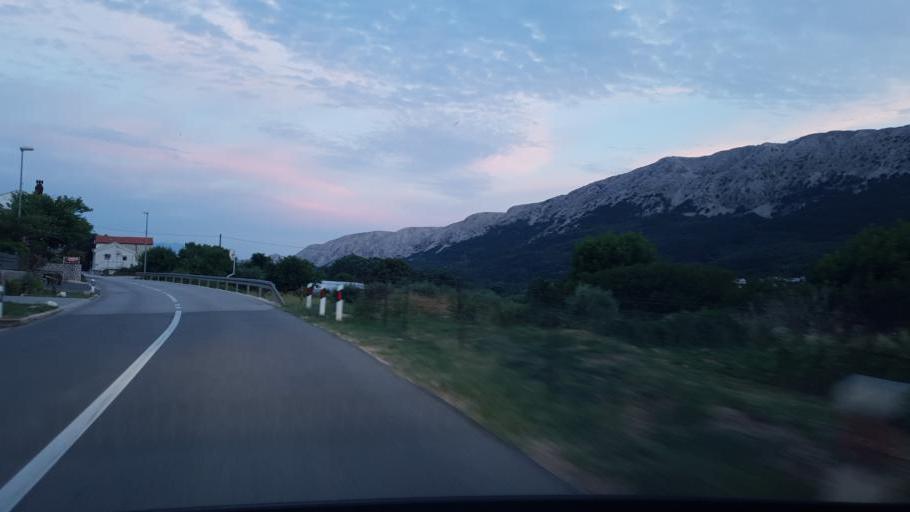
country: HR
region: Primorsko-Goranska
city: Punat
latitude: 44.9806
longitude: 14.7312
